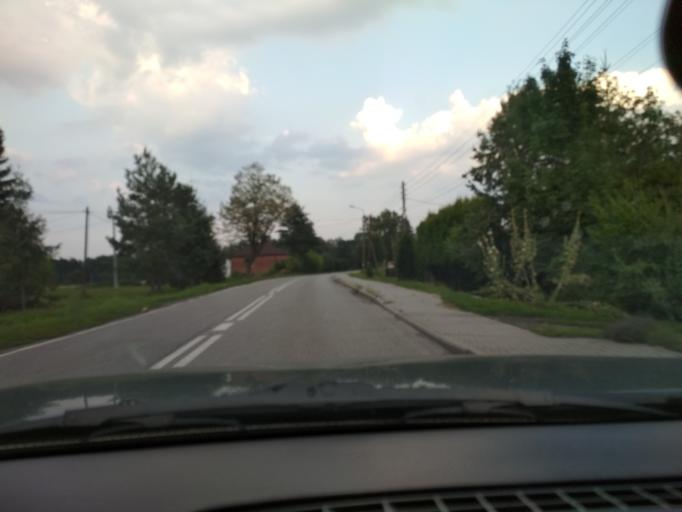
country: PL
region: Silesian Voivodeship
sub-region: Powiat cieszynski
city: Zablocie
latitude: 49.9017
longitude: 18.7841
